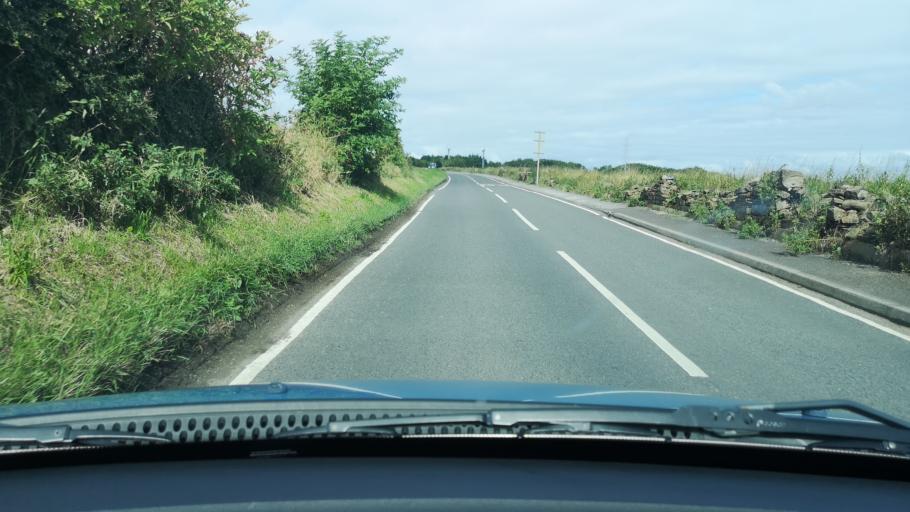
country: GB
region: England
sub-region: City and Borough of Wakefield
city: Horbury
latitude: 53.6446
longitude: -1.5585
